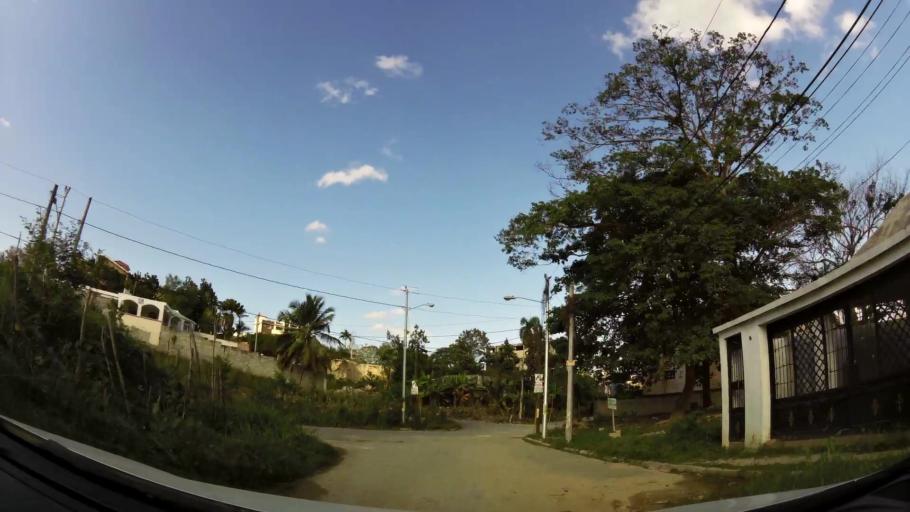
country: DO
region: Nacional
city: Ensanche Luperon
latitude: 18.5473
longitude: -69.9112
